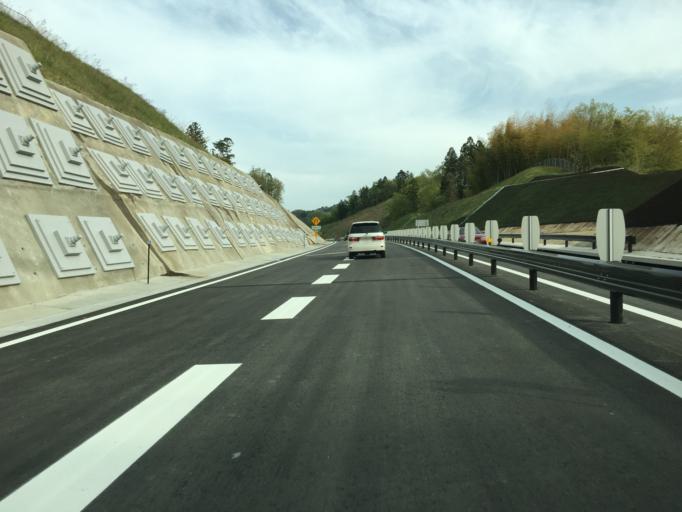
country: JP
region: Fukushima
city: Hobaramachi
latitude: 37.7932
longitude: 140.5505
